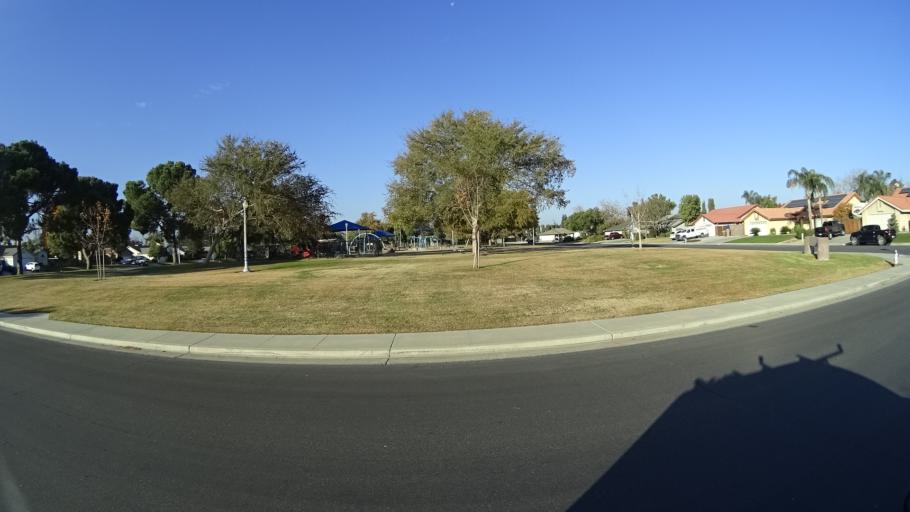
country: US
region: California
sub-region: Kern County
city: Rosedale
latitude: 35.3518
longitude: -119.1571
